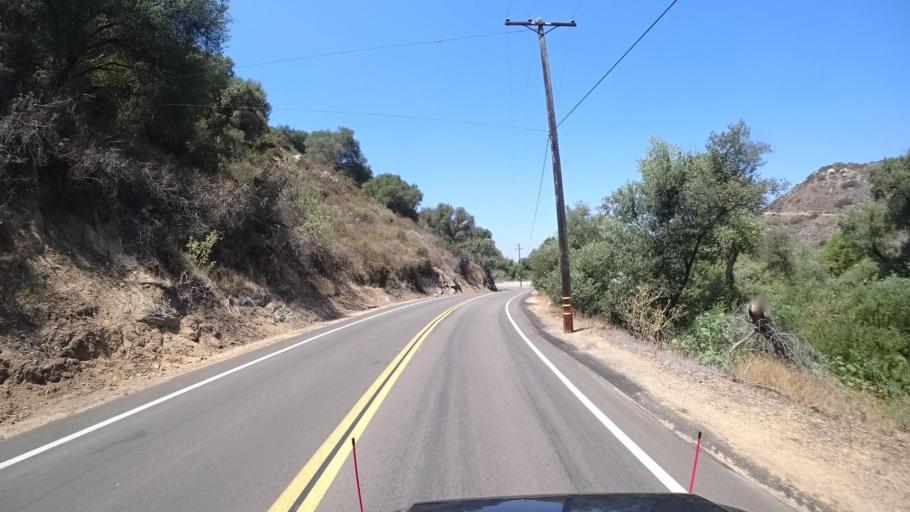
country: US
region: California
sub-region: San Diego County
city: Hidden Meadows
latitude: 33.2667
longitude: -117.1635
